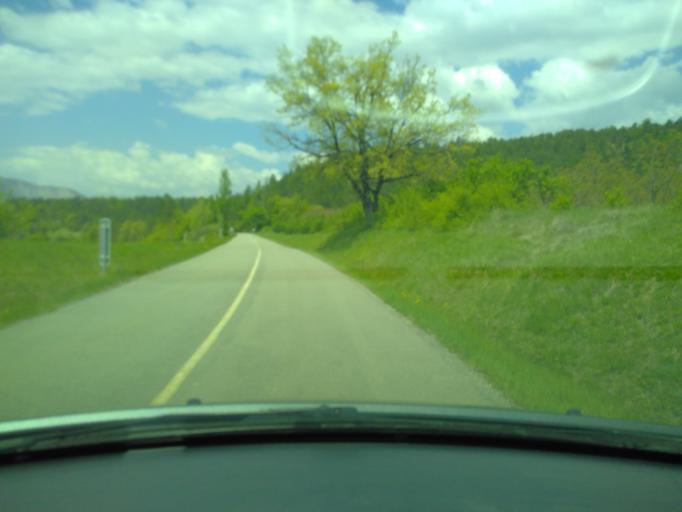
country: FR
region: Rhone-Alpes
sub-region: Departement de la Drome
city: Die
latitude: 44.6404
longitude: 5.4376
